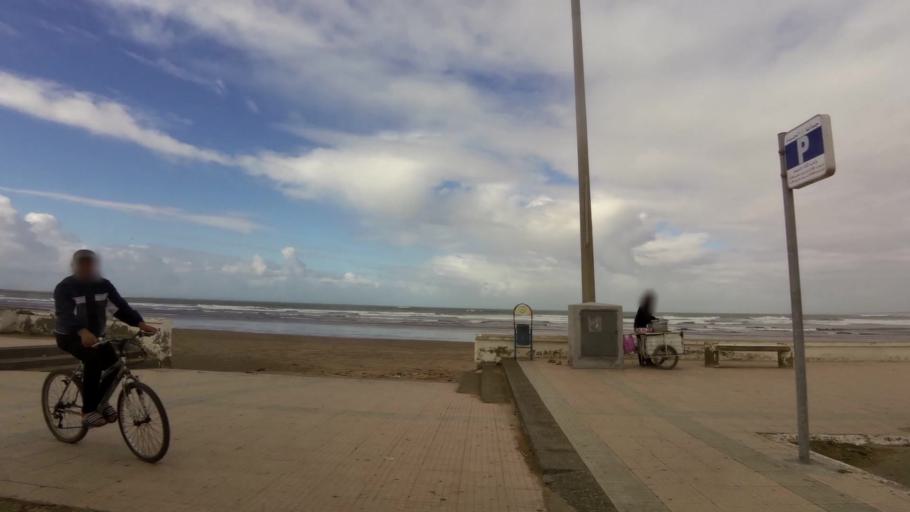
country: MA
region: Doukkala-Abda
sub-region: El-Jadida
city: El Jadida
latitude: 33.2461
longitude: -8.4921
